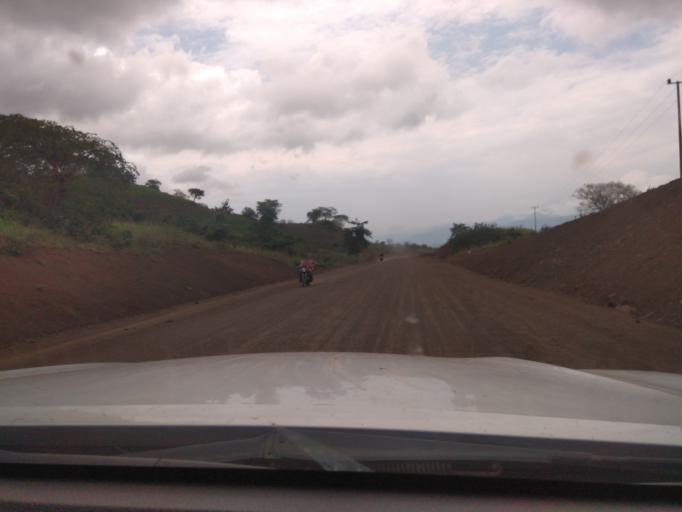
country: ET
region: Southern Nations, Nationalities, and People's Region
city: Felege Neway
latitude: 6.3929
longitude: 37.0713
